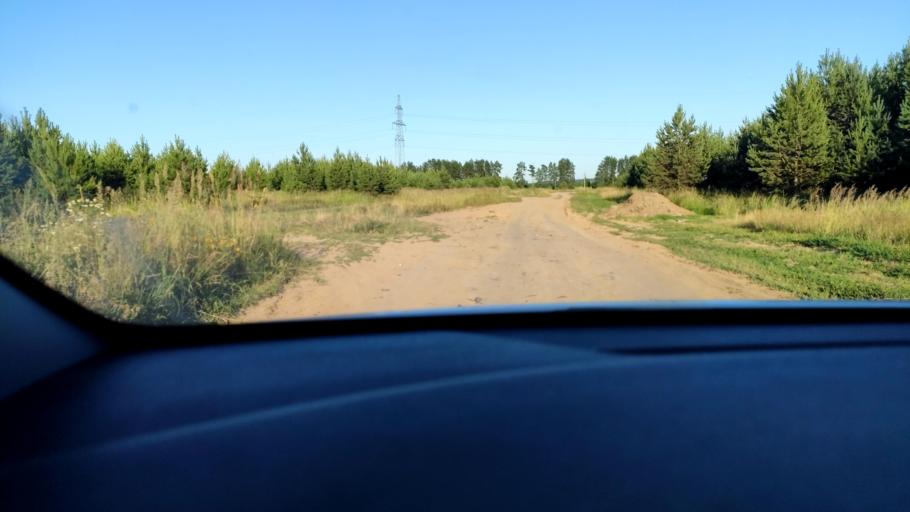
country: RU
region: Tatarstan
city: Vysokaya Gora
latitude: 55.8220
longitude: 49.2454
